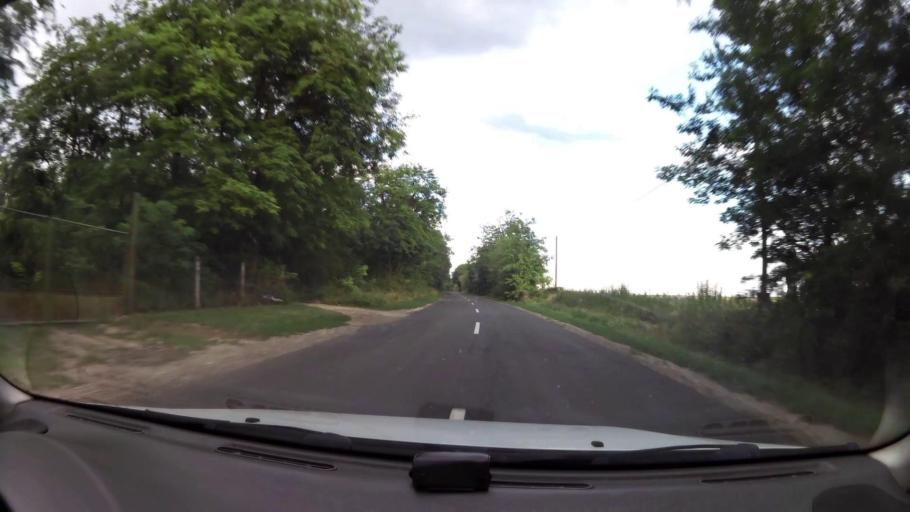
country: HU
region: Pest
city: Tapiobicske
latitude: 47.3515
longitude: 19.7070
